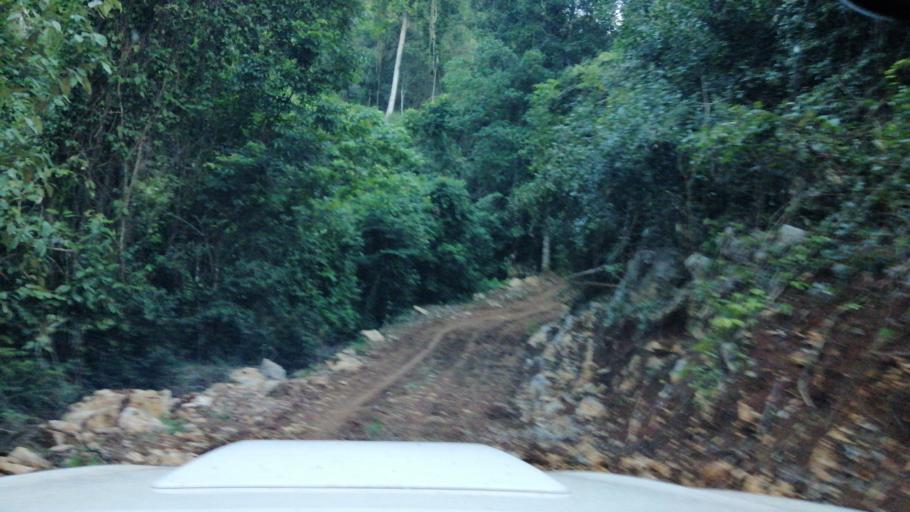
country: TH
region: Nan
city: Chaloem Phra Kiat
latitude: 19.7625
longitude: 101.1209
